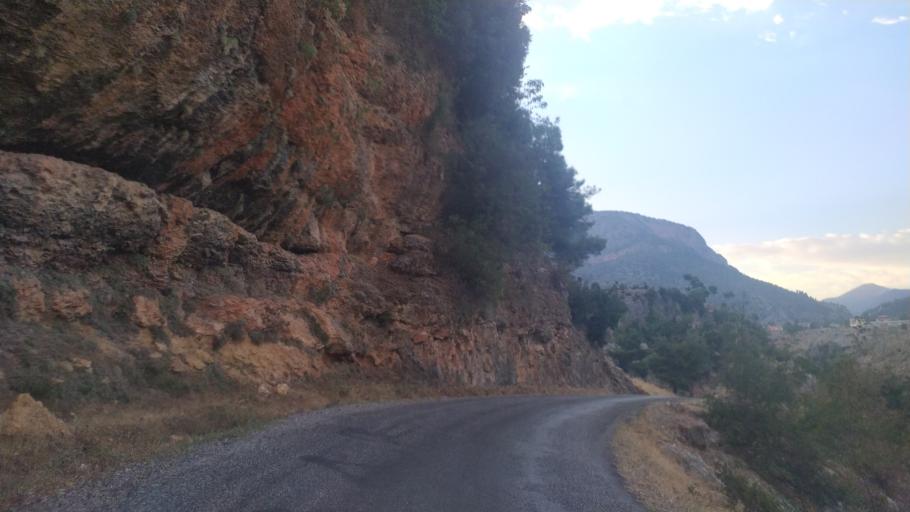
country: TR
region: Mersin
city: Camliyayla
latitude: 37.2381
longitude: 34.7144
